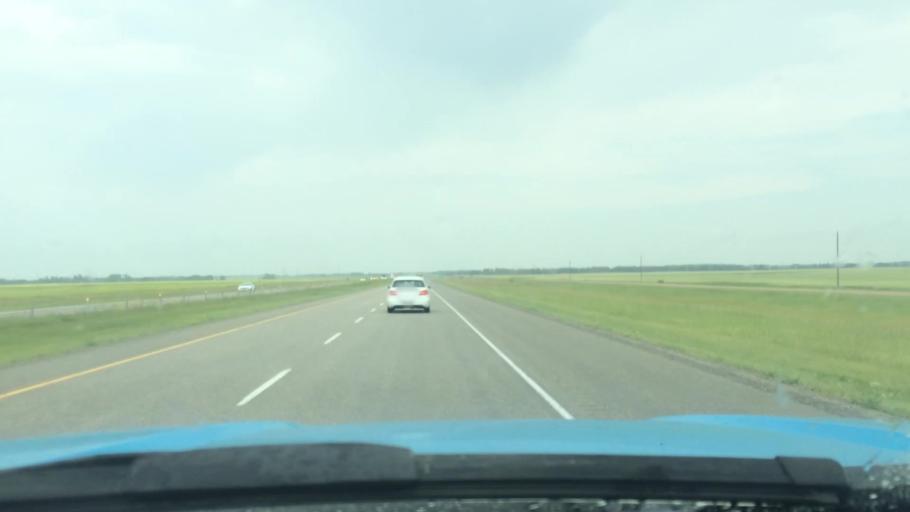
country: CA
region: Alberta
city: Olds
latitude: 51.7316
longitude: -114.0255
